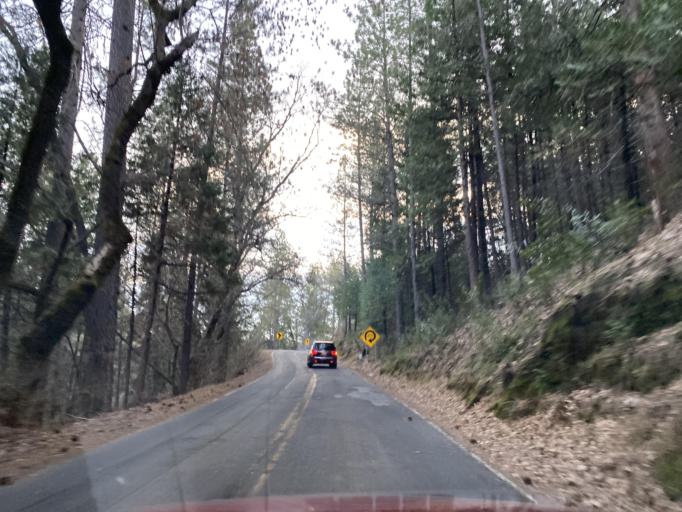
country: US
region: California
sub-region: Amador County
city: Pine Grove
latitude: 38.4981
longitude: -120.6985
